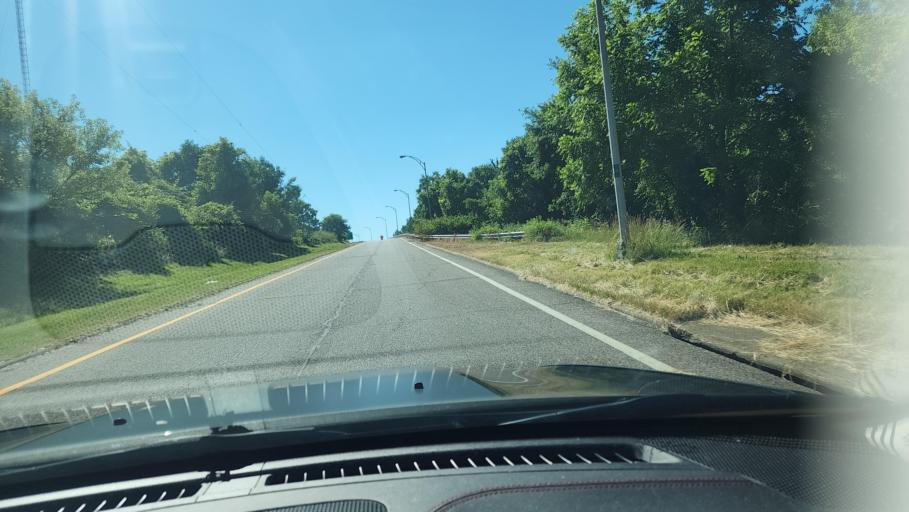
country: US
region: Ohio
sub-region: Mahoning County
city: Youngstown
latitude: 41.0807
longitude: -80.6348
